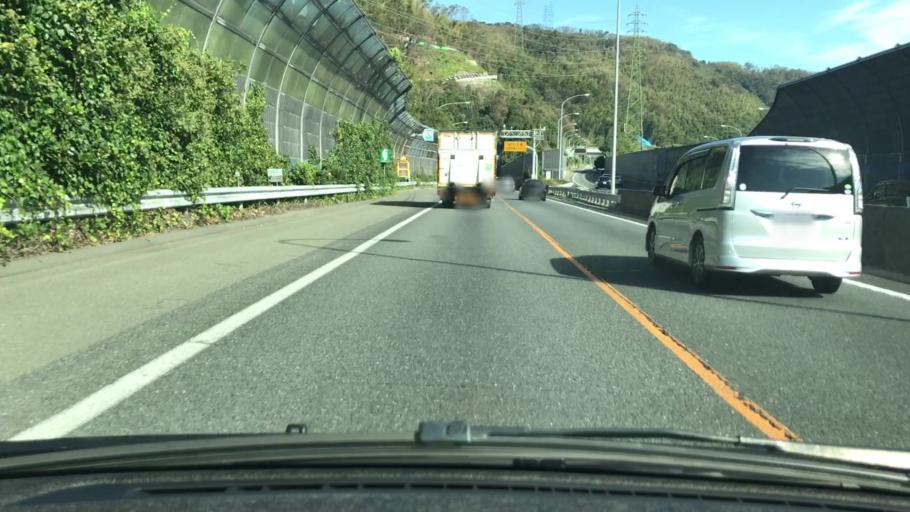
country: JP
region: Kyoto
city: Yawata
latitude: 34.8902
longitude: 135.6644
